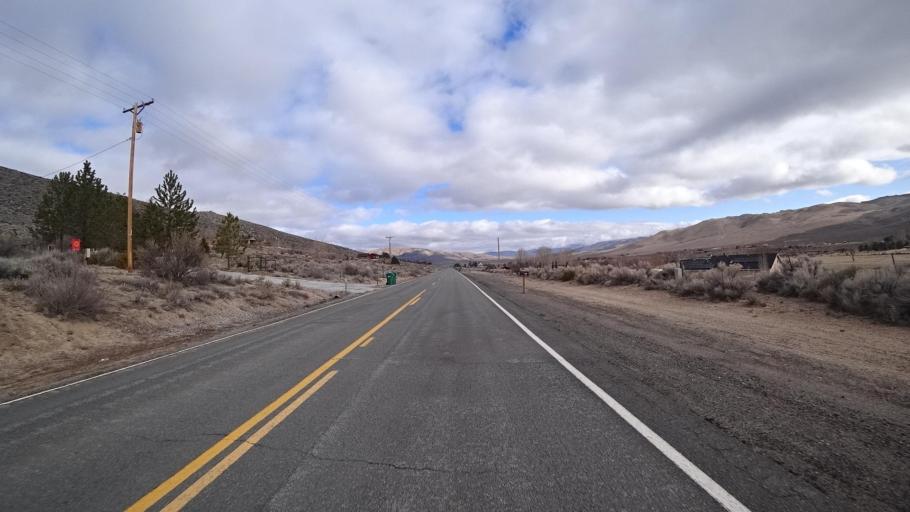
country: US
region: Nevada
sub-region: Washoe County
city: Cold Springs
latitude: 39.8480
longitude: -119.9353
